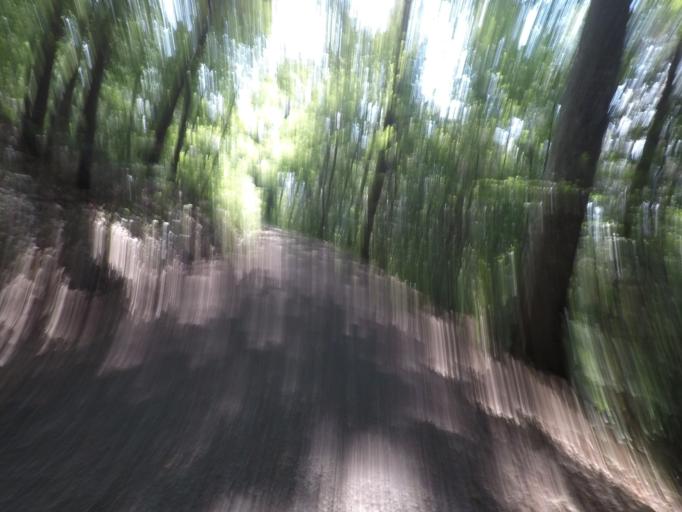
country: DE
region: Baden-Wuerttemberg
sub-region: Regierungsbezirk Stuttgart
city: Steinenbronn
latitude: 48.6542
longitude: 9.1061
